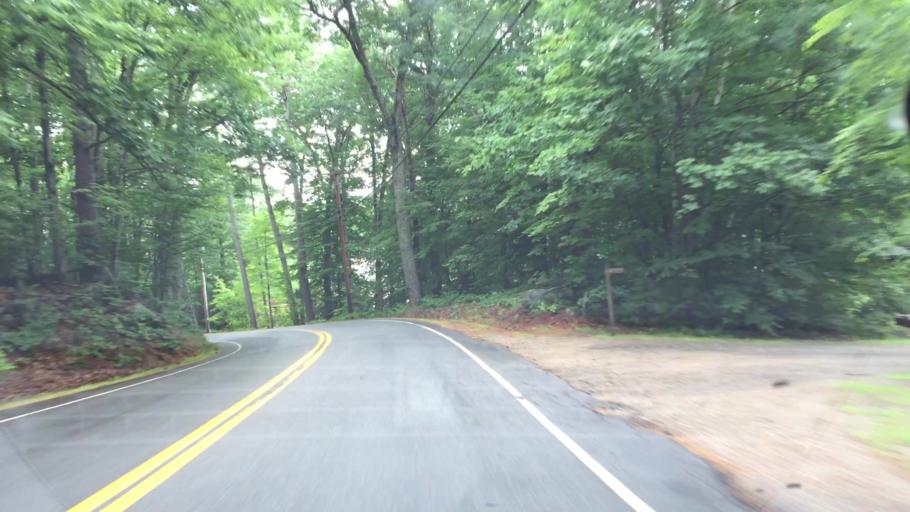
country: US
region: New Hampshire
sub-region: Carroll County
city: Center Harbor
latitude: 43.7320
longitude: -71.4757
